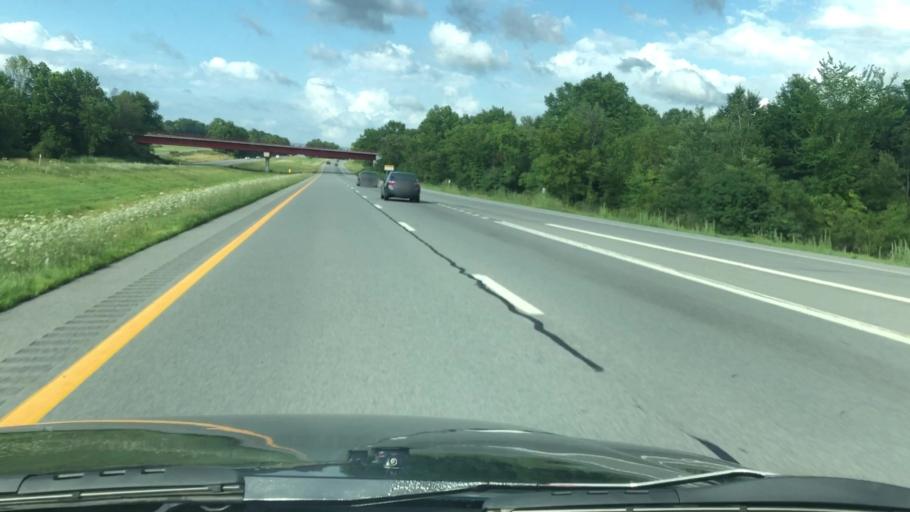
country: US
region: New York
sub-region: Orange County
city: Mechanicstown
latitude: 41.4279
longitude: -74.3926
